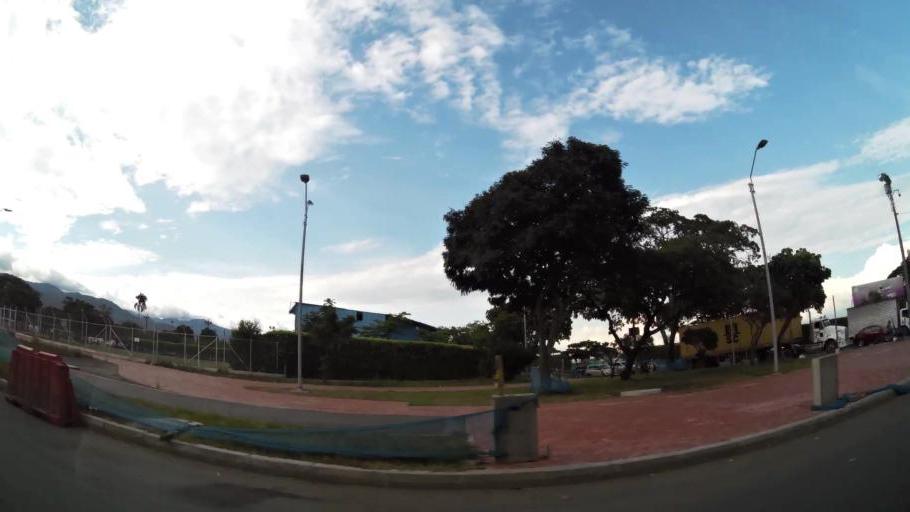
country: CO
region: Valle del Cauca
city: Cali
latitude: 3.4534
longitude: -76.5057
